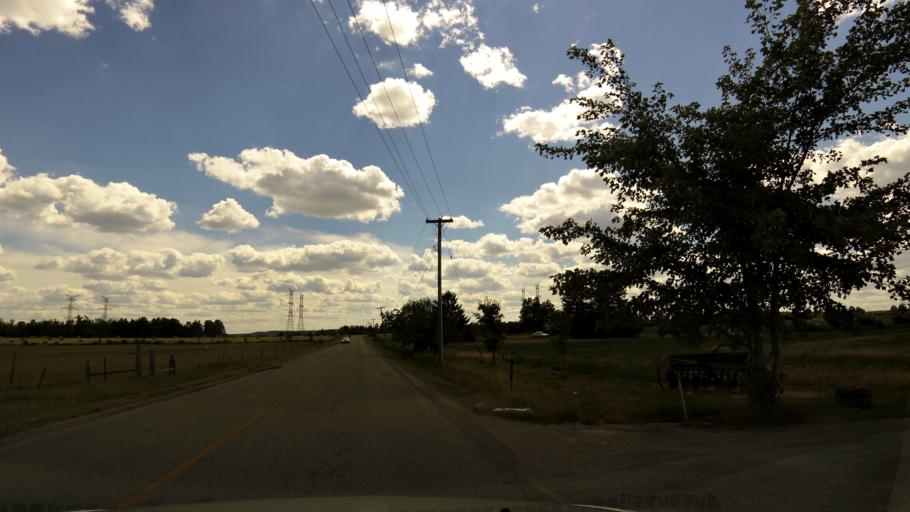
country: CA
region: Ontario
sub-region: Halton
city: Milton
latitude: 43.5878
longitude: -79.9178
